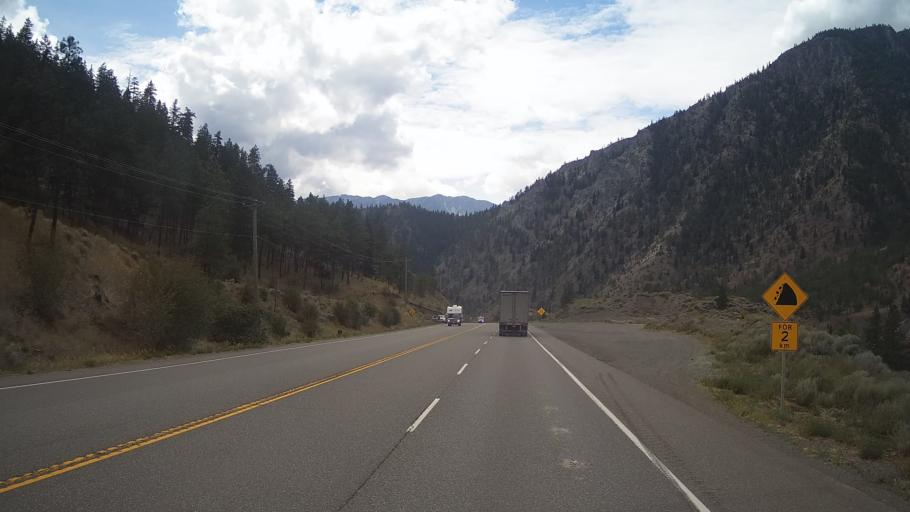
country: CA
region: British Columbia
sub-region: Thompson-Nicola Regional District
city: Ashcroft
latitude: 50.2885
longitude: -121.3984
